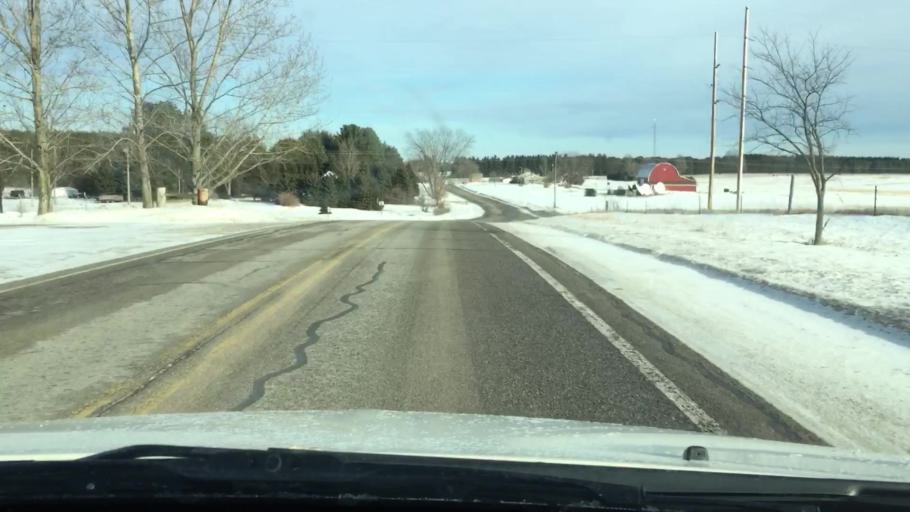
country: US
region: Michigan
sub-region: Kalkaska County
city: Kalkaska
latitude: 44.6404
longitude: -85.2118
